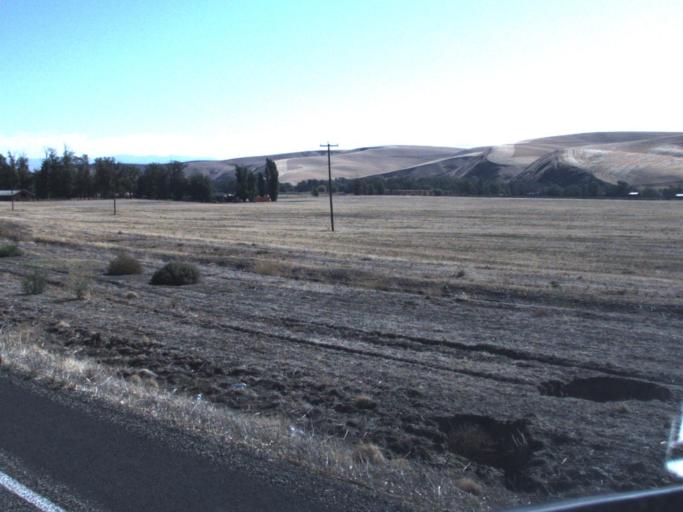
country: US
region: Washington
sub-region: Walla Walla County
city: Waitsburg
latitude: 46.2979
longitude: -118.2798
